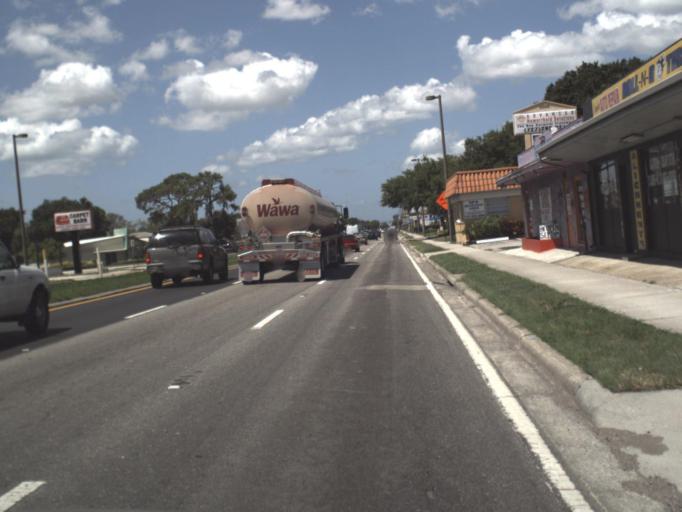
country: US
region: Florida
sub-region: Pinellas County
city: Pinellas Park
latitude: 27.8393
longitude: -82.7048
